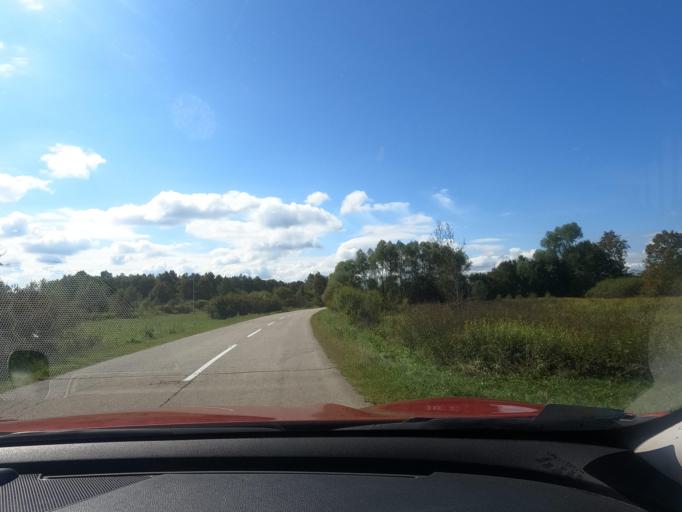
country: BA
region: Federation of Bosnia and Herzegovina
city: Vrnograc
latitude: 45.2532
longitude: 15.9447
